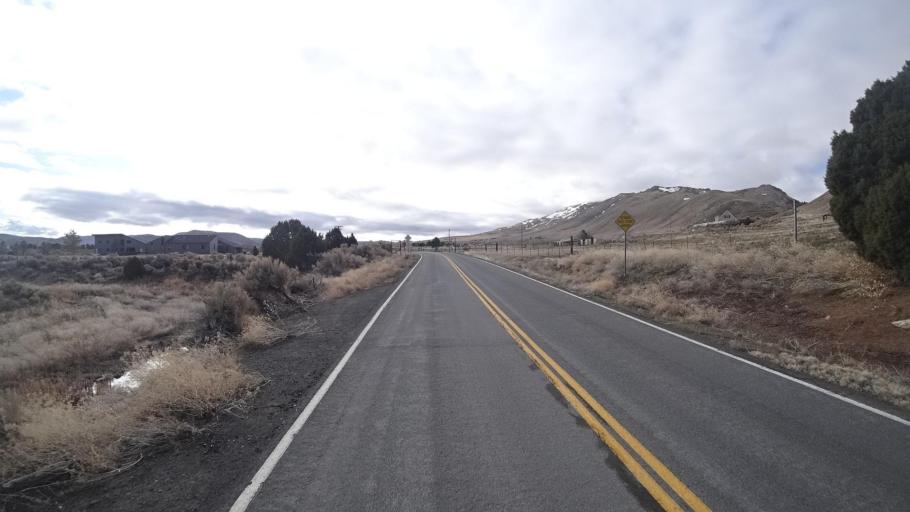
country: US
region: Nevada
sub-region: Washoe County
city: Cold Springs
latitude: 39.9012
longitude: -119.9868
